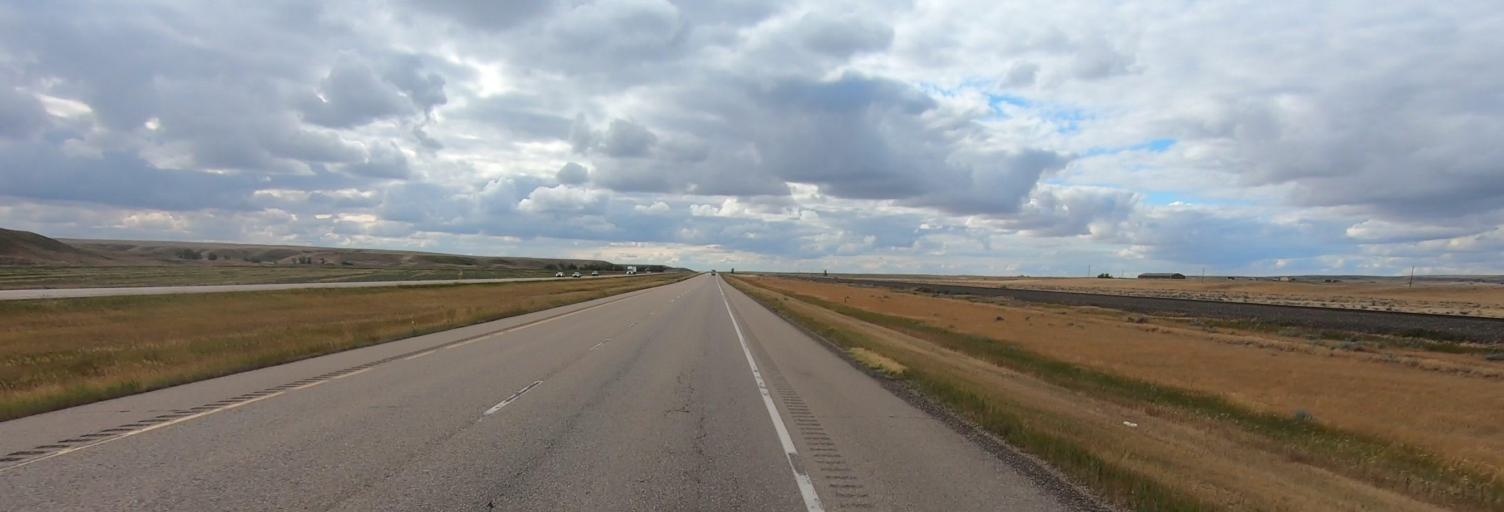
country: CA
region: Alberta
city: Medicine Hat
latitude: 49.9404
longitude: -110.1775
